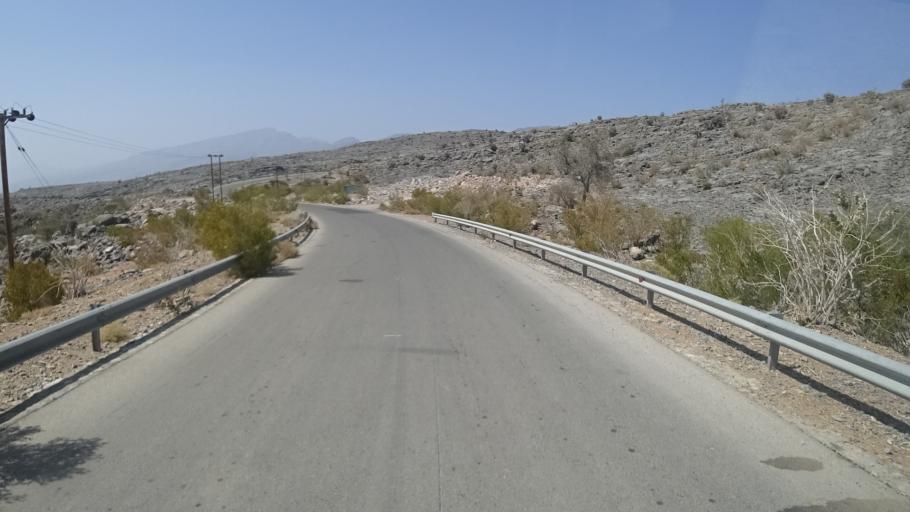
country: OM
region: Muhafazat ad Dakhiliyah
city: Bahla'
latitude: 23.1245
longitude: 57.4051
